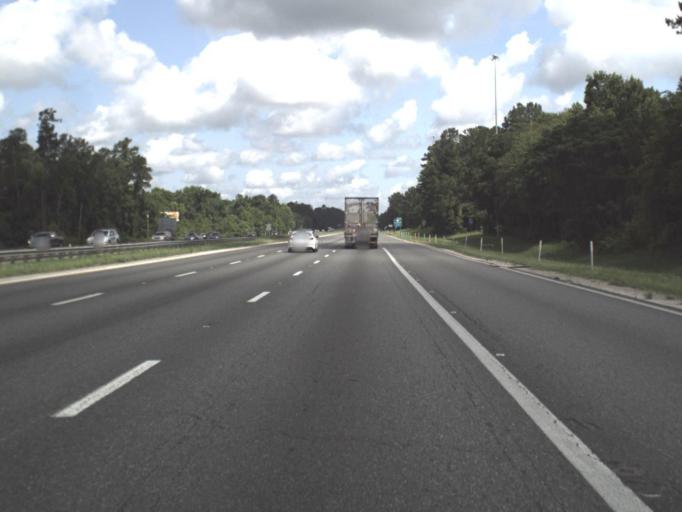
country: US
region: Florida
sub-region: Alachua County
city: Gainesville
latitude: 29.6047
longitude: -82.3754
